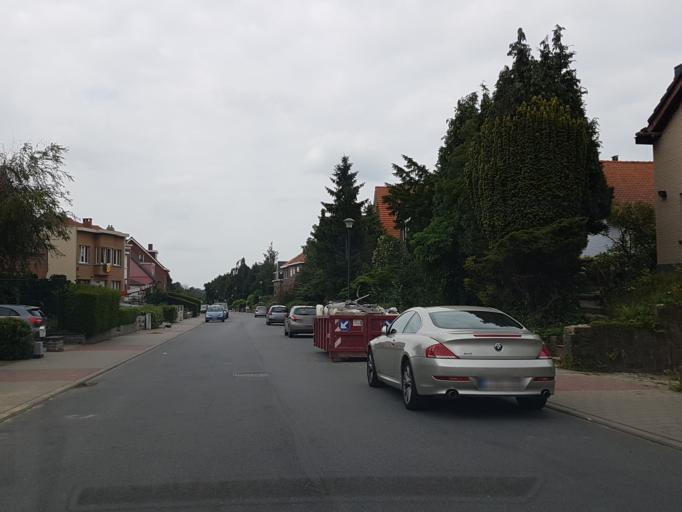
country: BE
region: Flanders
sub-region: Provincie Vlaams-Brabant
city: Kraainem
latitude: 50.8681
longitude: 4.4418
